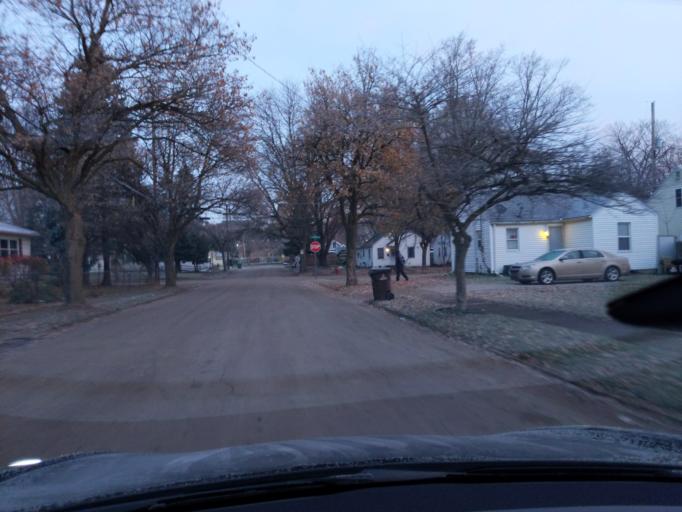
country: US
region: Michigan
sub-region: Ingham County
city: Lansing
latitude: 42.7009
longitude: -84.5553
